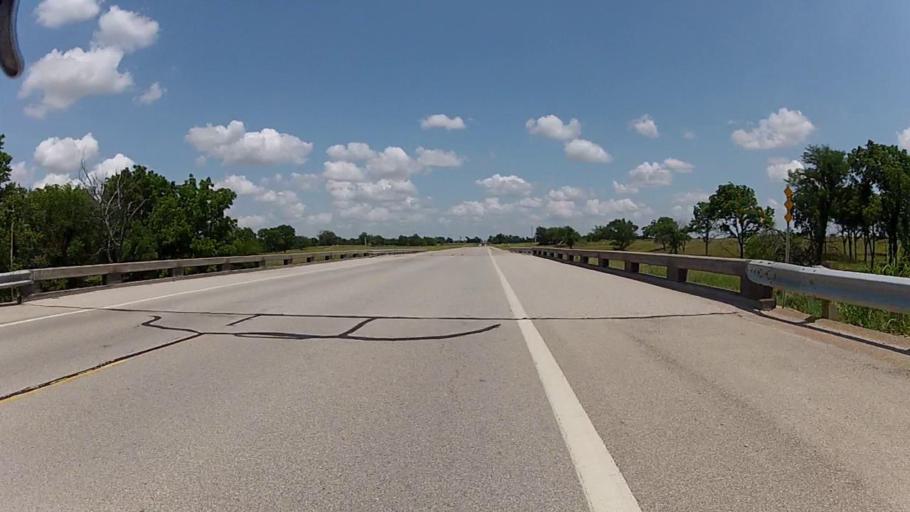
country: US
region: Kansas
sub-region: Labette County
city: Altamont
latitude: 37.1926
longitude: -95.3787
